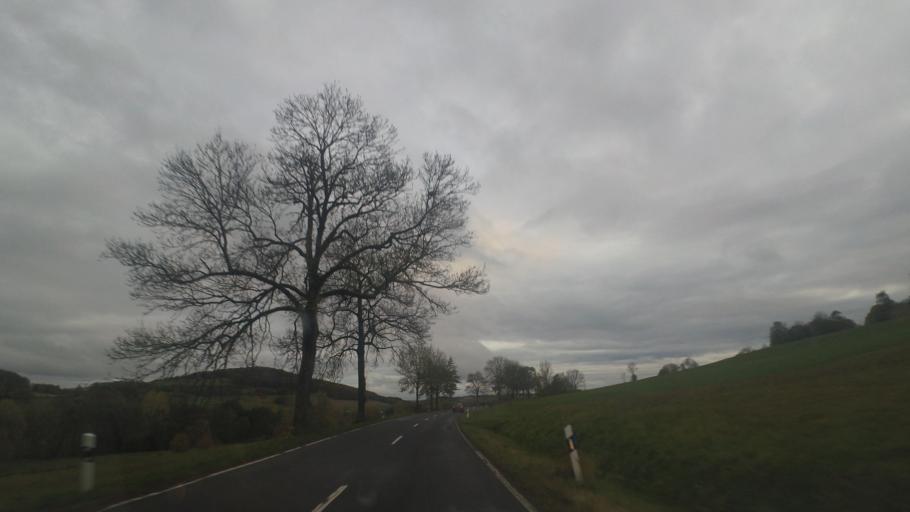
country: DE
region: Hesse
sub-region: Regierungsbezirk Giessen
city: Freiensteinau
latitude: 50.4112
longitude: 9.4206
